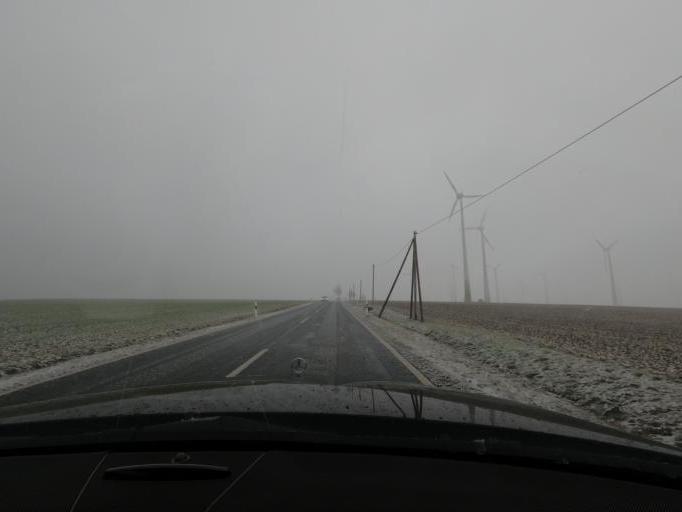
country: DE
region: Thuringia
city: Buttstedt
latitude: 51.2323
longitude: 10.2957
